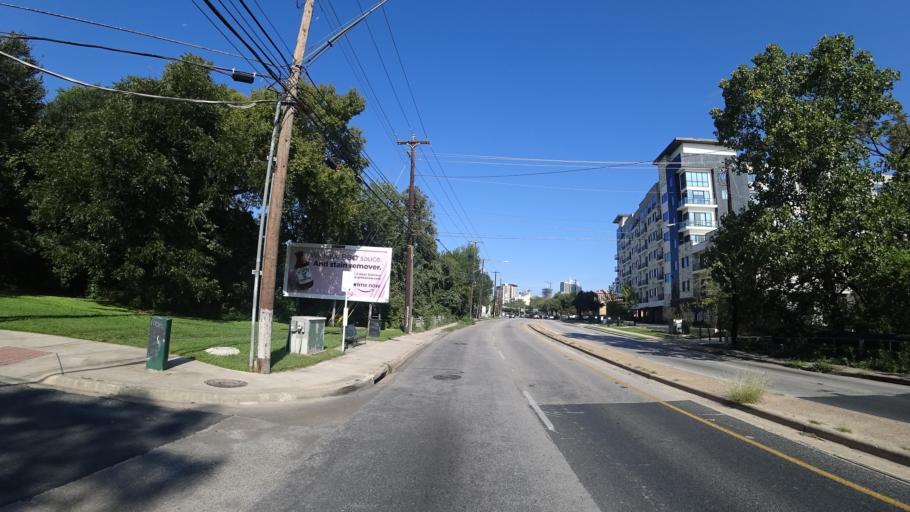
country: US
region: Texas
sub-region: Travis County
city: Austin
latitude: 30.2535
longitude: -97.7439
